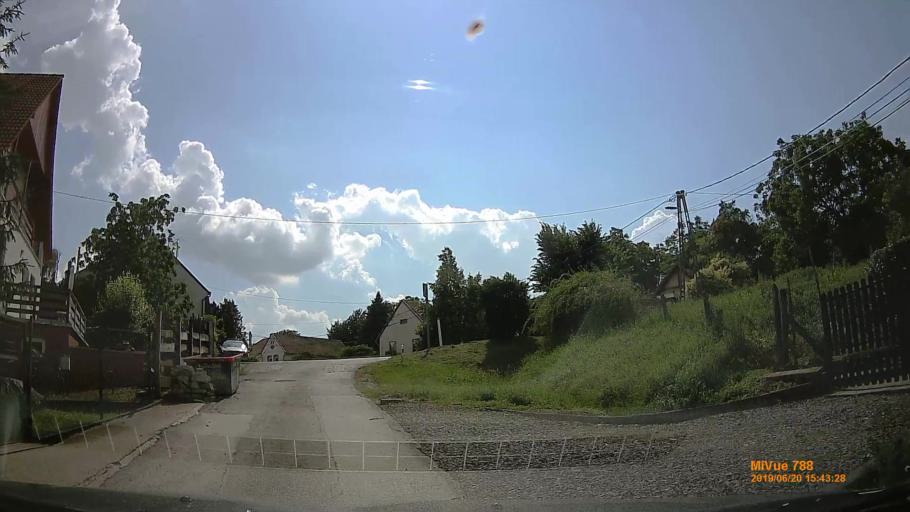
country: HU
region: Baranya
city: Kozarmisleny
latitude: 45.9830
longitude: 18.2617
